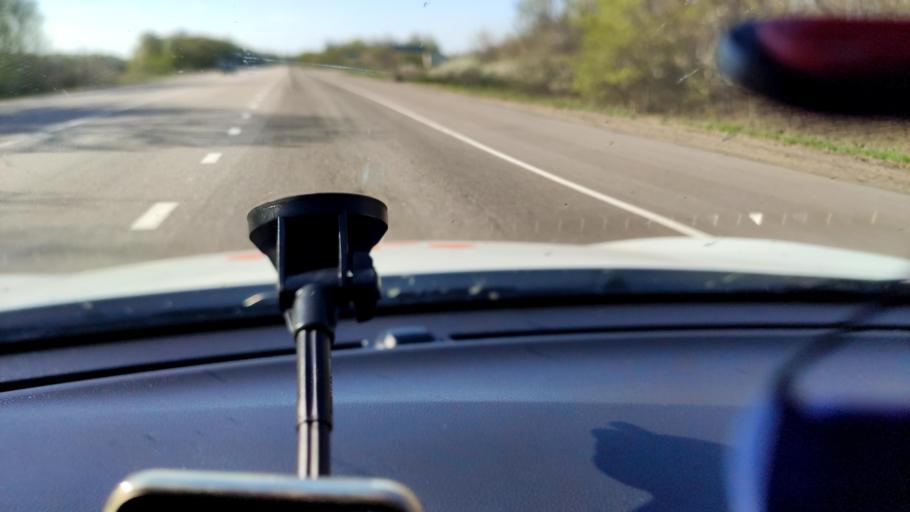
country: RU
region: Voronezj
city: Kolodeznyy
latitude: 51.3090
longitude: 39.0361
